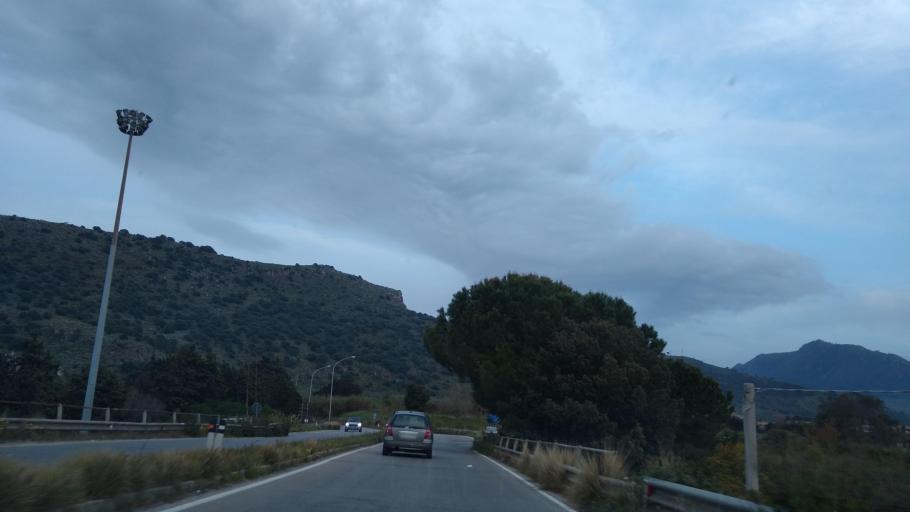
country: IT
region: Sicily
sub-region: Palermo
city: Partinico
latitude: 38.0361
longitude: 13.1124
